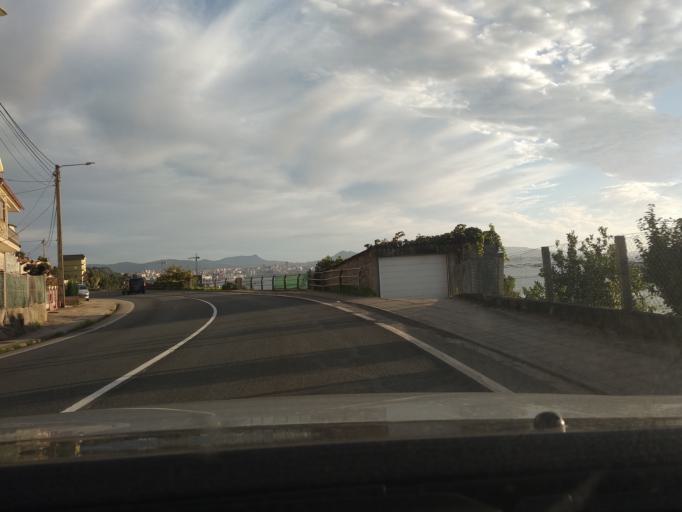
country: ES
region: Galicia
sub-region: Provincia de Pontevedra
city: Moana
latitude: 42.2859
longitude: -8.7152
